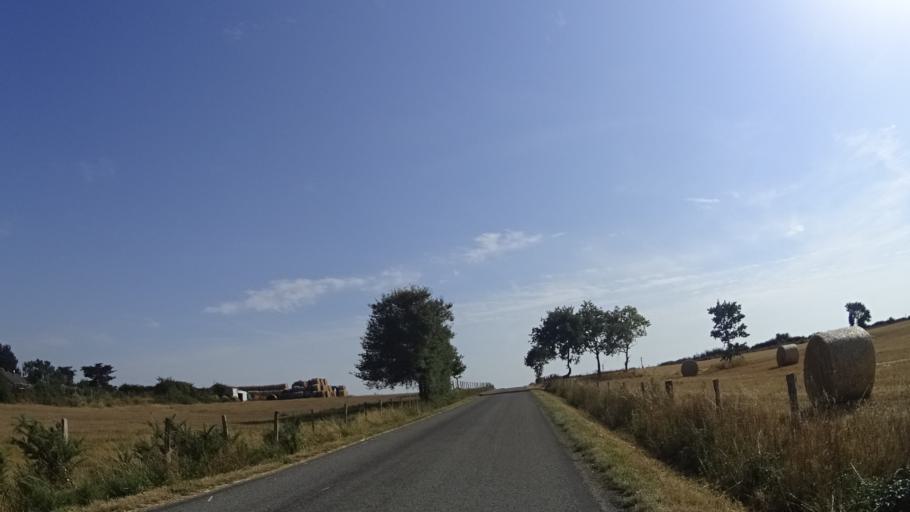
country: FR
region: Pays de la Loire
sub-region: Departement de la Loire-Atlantique
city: Donges
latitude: 47.3283
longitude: -2.0447
